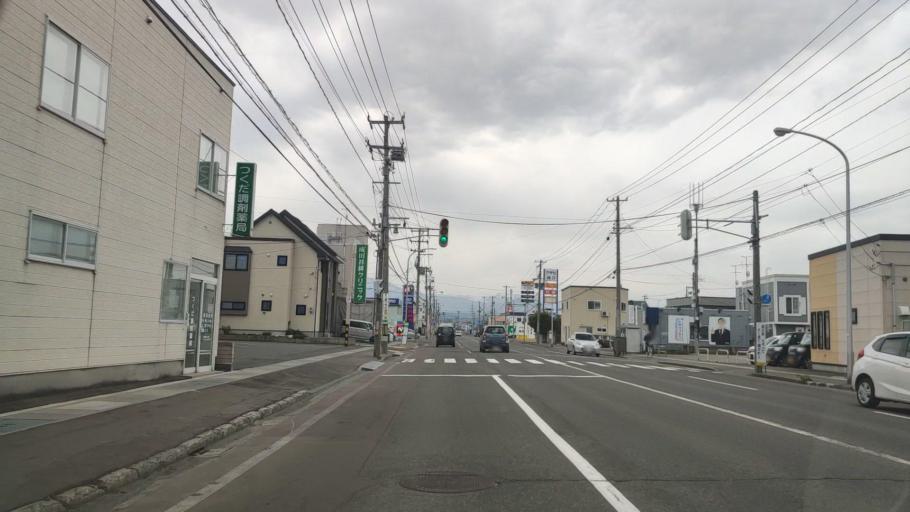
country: JP
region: Aomori
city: Aomori Shi
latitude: 40.8165
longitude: 140.7751
